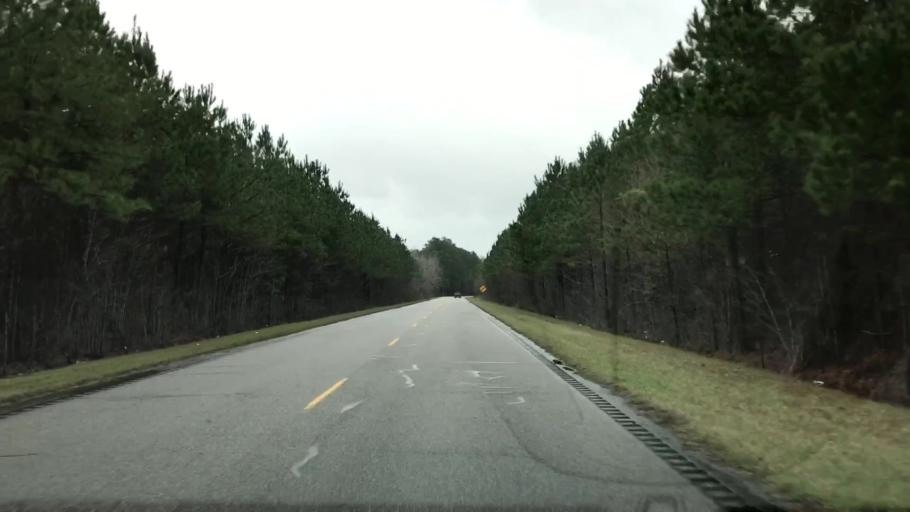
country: US
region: South Carolina
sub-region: Williamsburg County
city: Andrews
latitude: 33.5645
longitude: -79.4535
